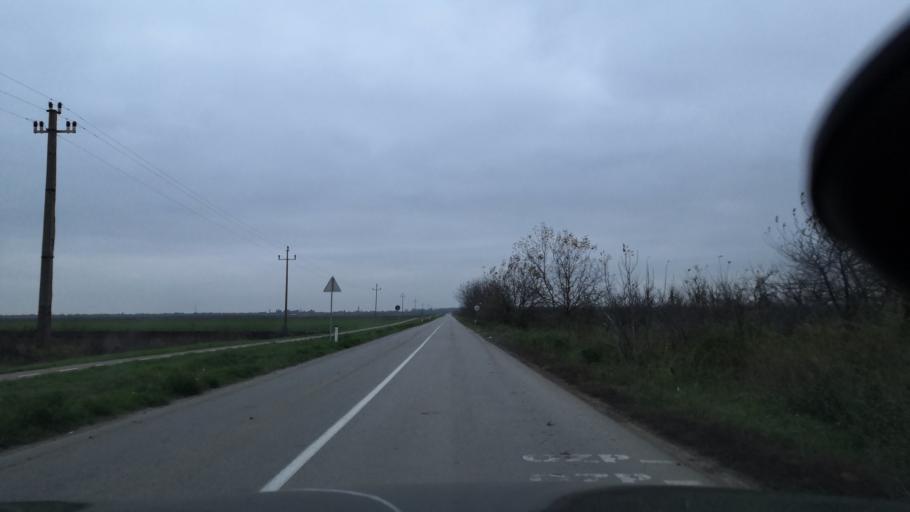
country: HU
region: Csongrad
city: Roszke
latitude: 46.1502
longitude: 20.1035
